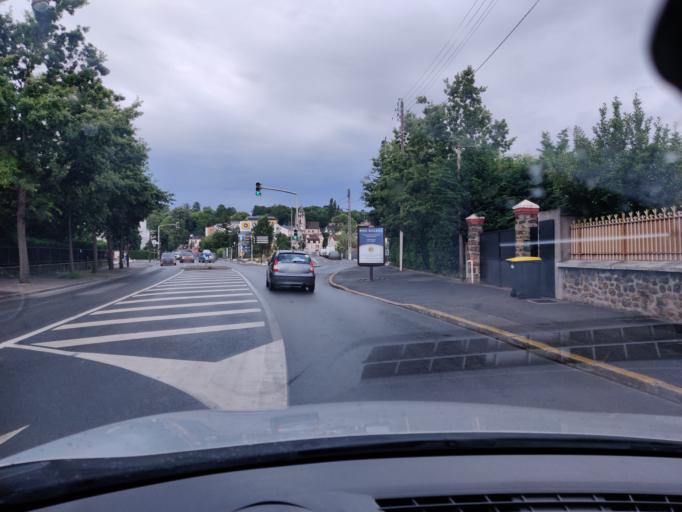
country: FR
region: Ile-de-France
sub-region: Departement de l'Essonne
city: Juvisy-sur-Orge
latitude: 48.6722
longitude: 2.3795
